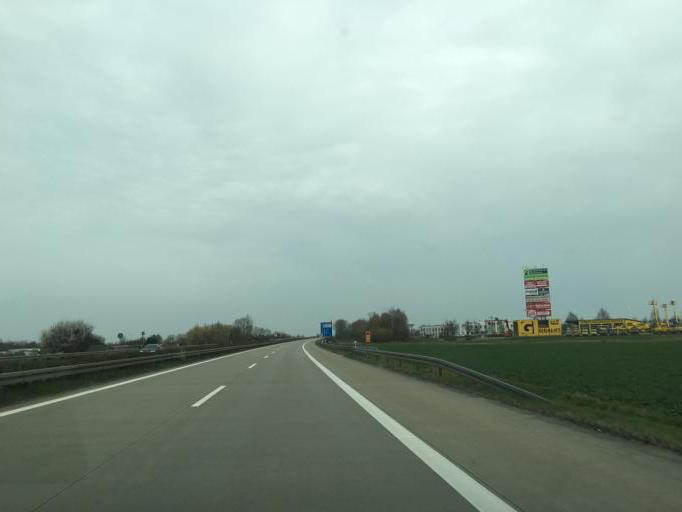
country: DE
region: Mecklenburg-Vorpommern
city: Roggentin
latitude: 54.0734
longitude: 12.1946
